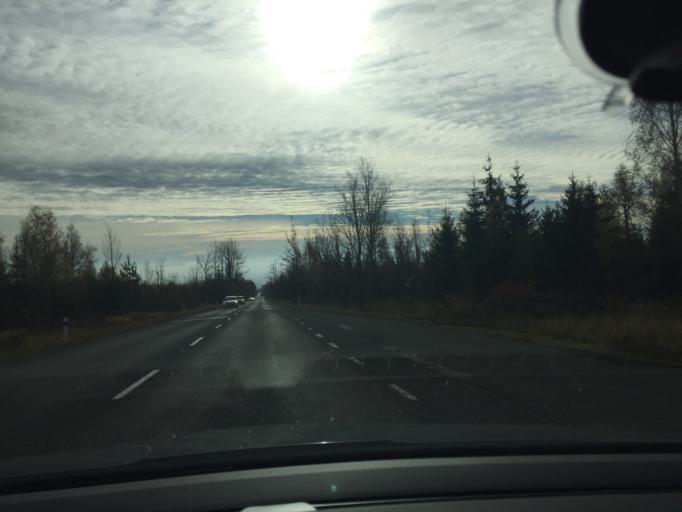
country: SK
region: Presovsky
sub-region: Okres Poprad
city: Vysoke Tatry
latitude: 49.1310
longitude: 20.2367
